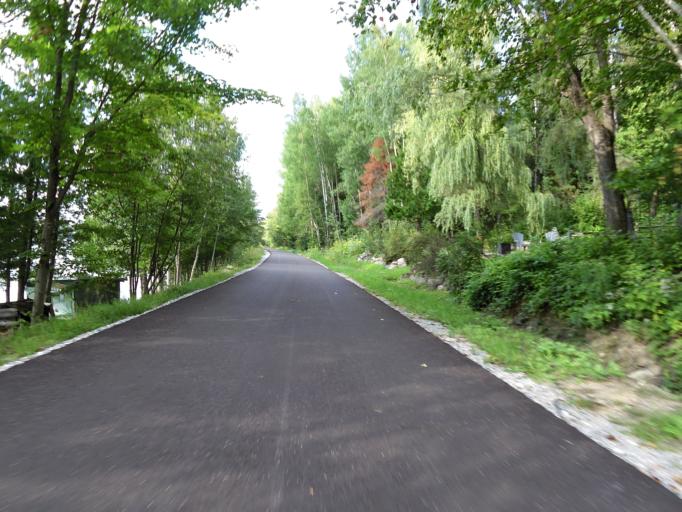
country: CA
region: Quebec
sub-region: Outaouais
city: Maniwaki
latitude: 46.2011
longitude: -76.0466
